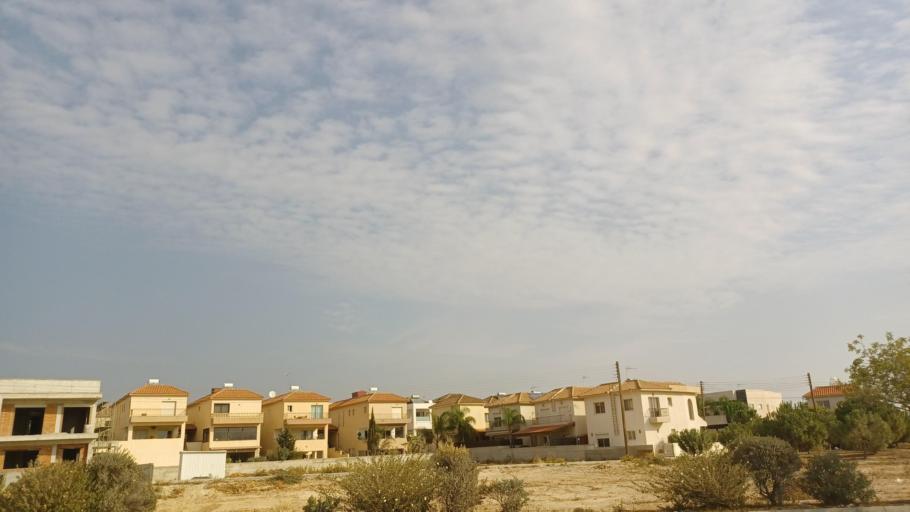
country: CY
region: Limassol
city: Ypsonas
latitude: 34.6946
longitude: 32.9427
